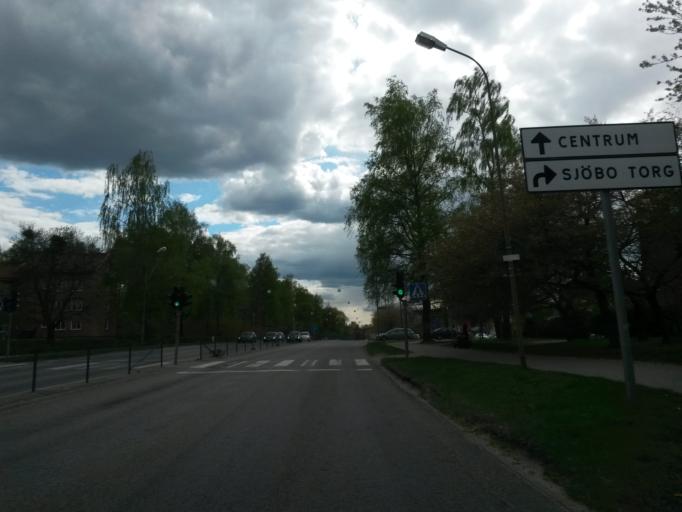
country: SE
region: Vaestra Goetaland
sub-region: Boras Kommun
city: Boras
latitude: 57.7500
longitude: 12.9457
